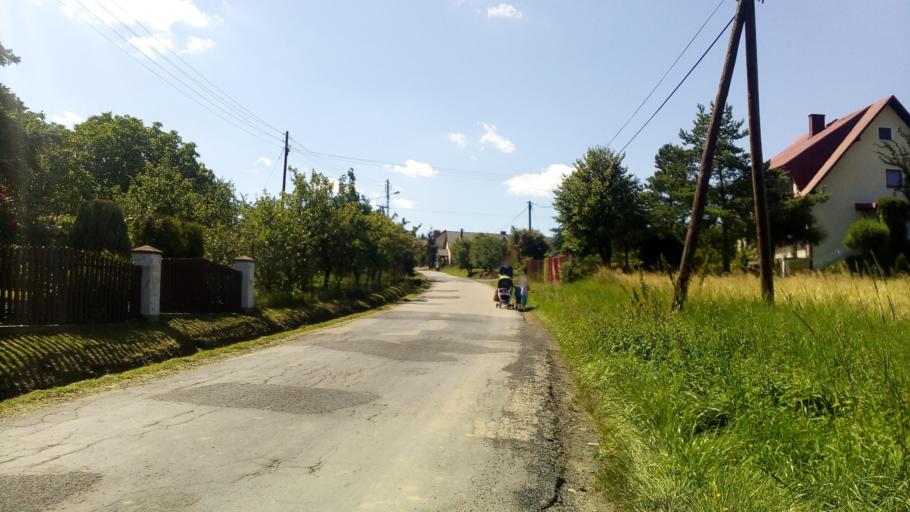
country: PL
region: Lesser Poland Voivodeship
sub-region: Powiat nowosadecki
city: Olszana
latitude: 49.5655
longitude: 20.4964
